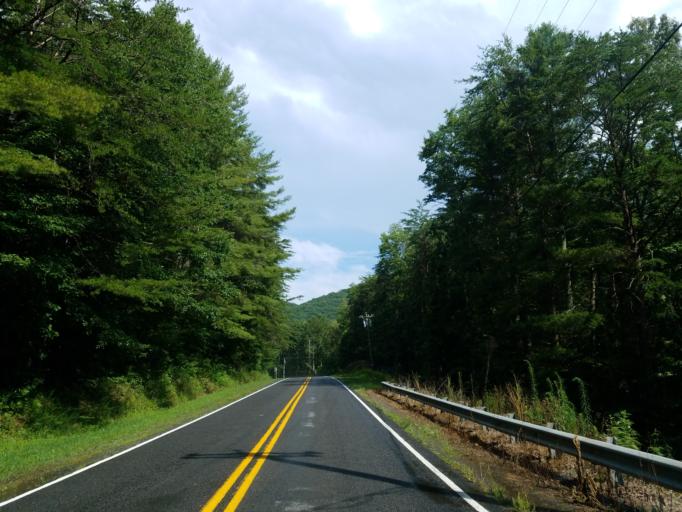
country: US
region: Georgia
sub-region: Fannin County
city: Blue Ridge
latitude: 34.6716
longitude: -84.2820
